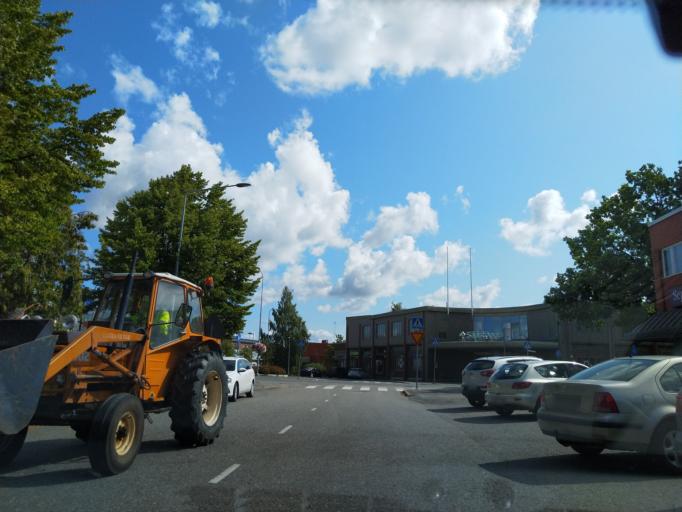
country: FI
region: Satakunta
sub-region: Pori
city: Huittinen
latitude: 61.1774
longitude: 22.6967
